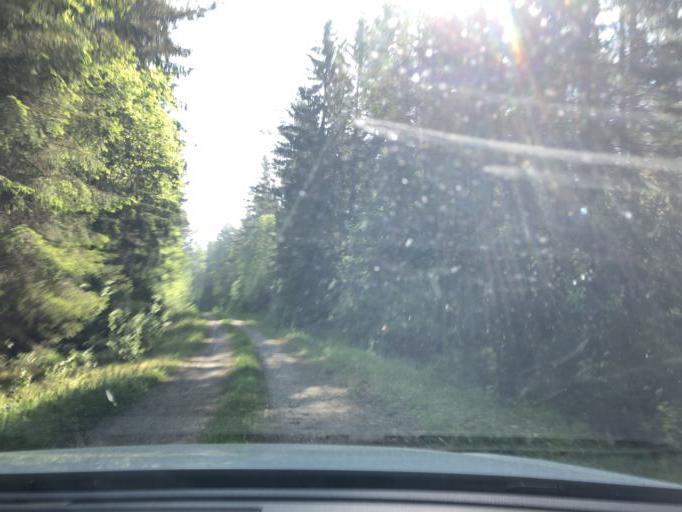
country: SE
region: Dalarna
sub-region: Avesta Kommun
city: Horndal
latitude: 60.2160
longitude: 16.4984
